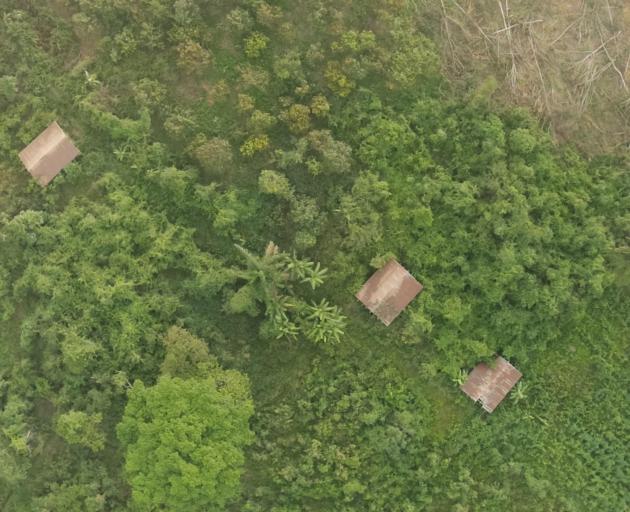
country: BO
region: La Paz
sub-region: Provincia Larecaja
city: Guanay
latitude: -15.7738
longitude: -67.6591
